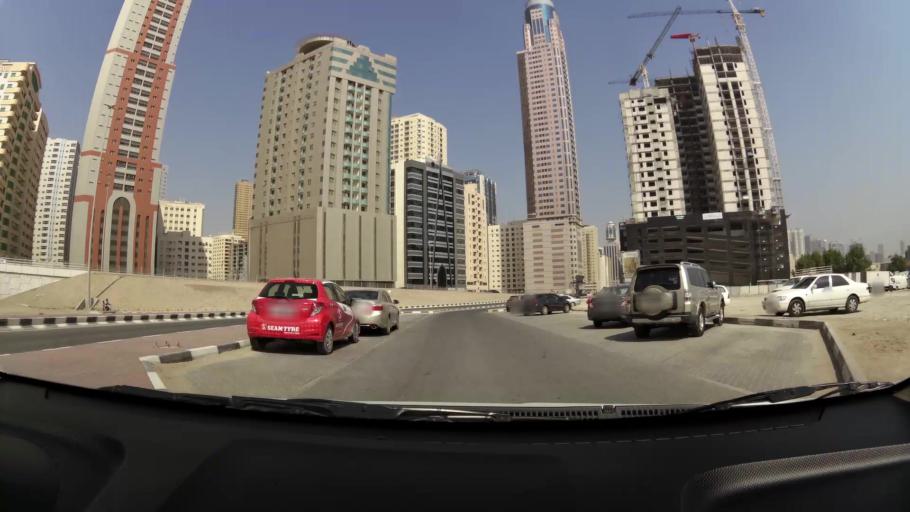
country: AE
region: Ash Shariqah
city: Sharjah
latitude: 25.3047
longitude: 55.3847
